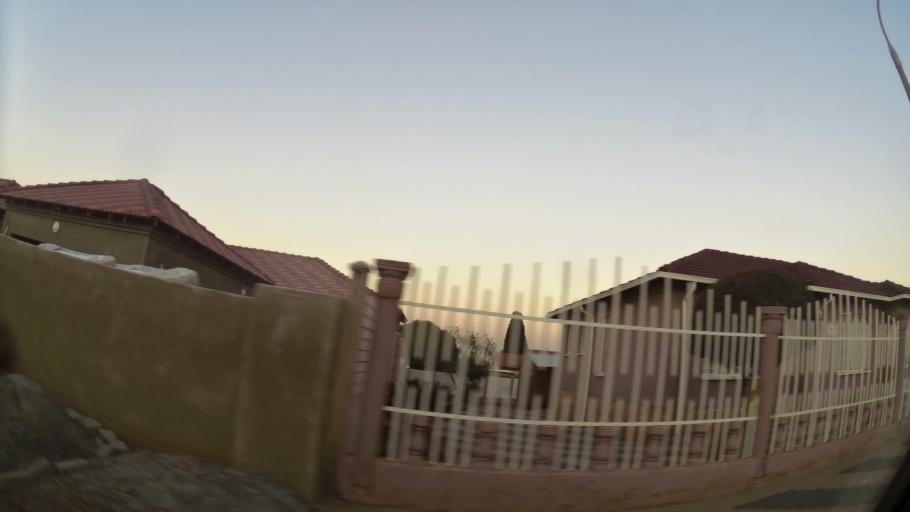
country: ZA
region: North-West
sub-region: Bojanala Platinum District Municipality
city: Rustenburg
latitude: -25.6552
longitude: 27.2063
